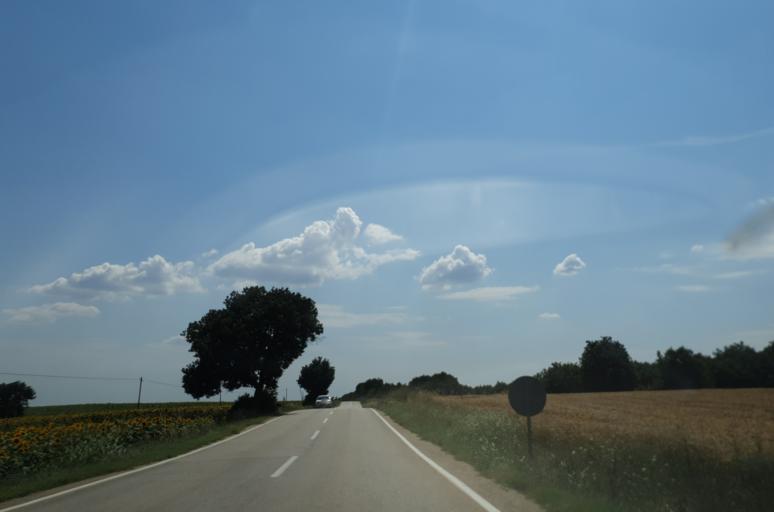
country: TR
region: Kirklareli
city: Vize
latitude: 41.4786
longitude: 27.6793
